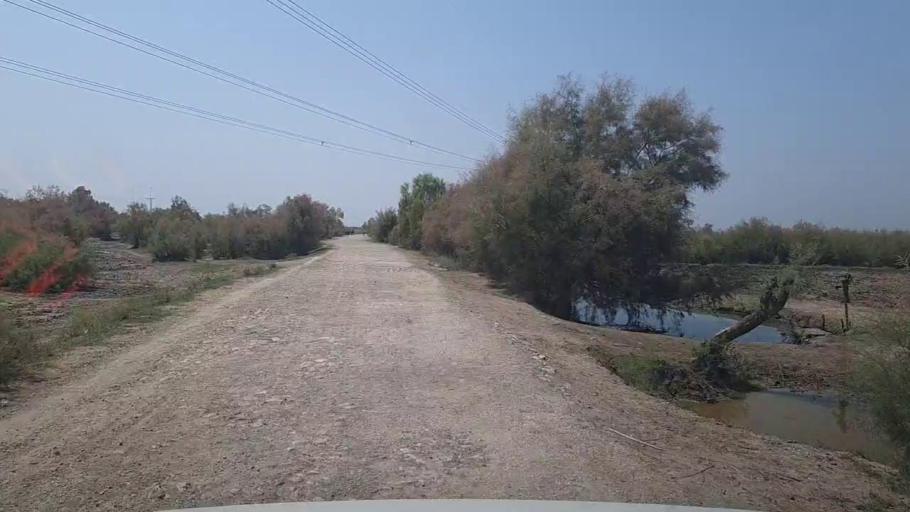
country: PK
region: Sindh
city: Kandhkot
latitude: 28.3130
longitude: 69.3603
